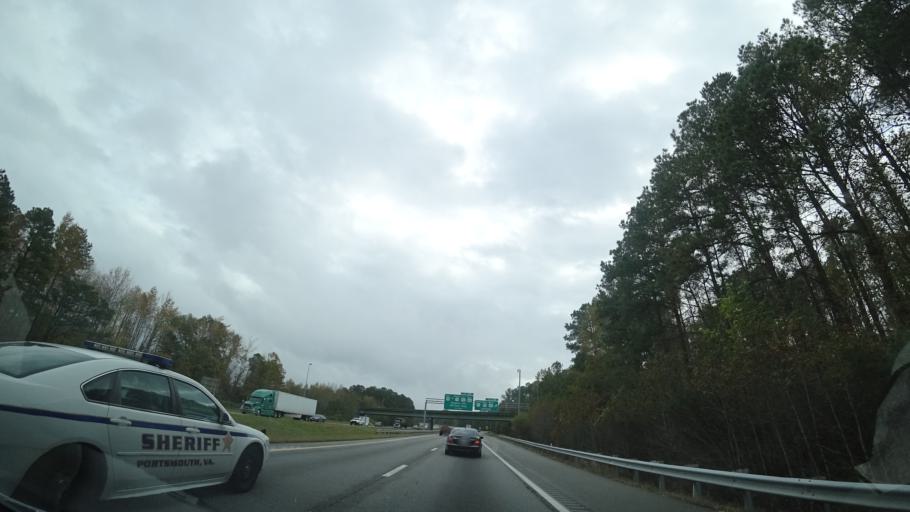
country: US
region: Virginia
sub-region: City of Portsmouth
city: Portsmouth Heights
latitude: 36.7928
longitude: -76.4269
